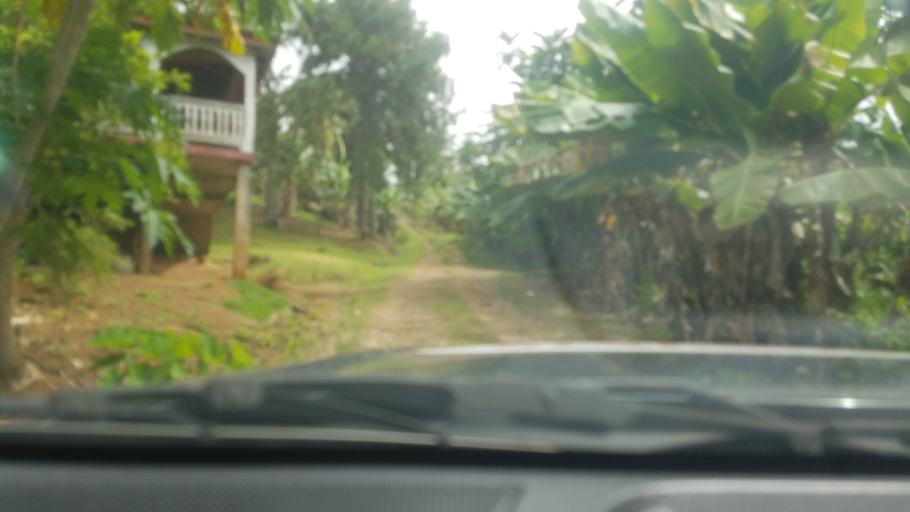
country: LC
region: Micoud Quarter
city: Micoud
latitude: 13.8030
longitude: -60.9324
